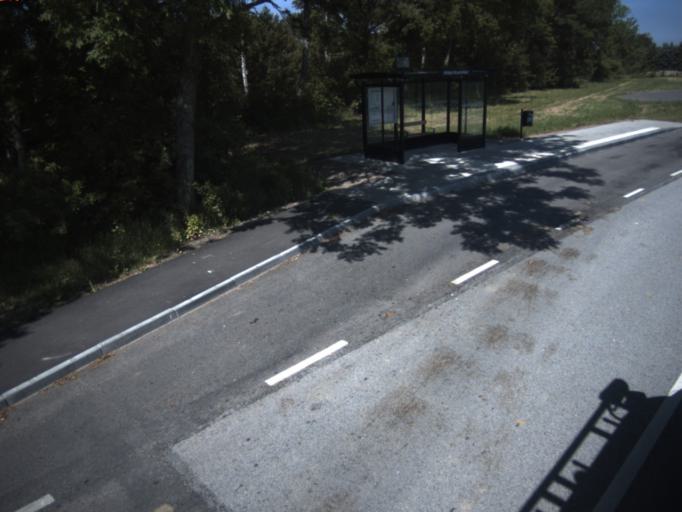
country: DK
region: Capital Region
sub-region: Helsingor Kommune
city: Helsingor
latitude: 56.1022
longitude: 12.6390
